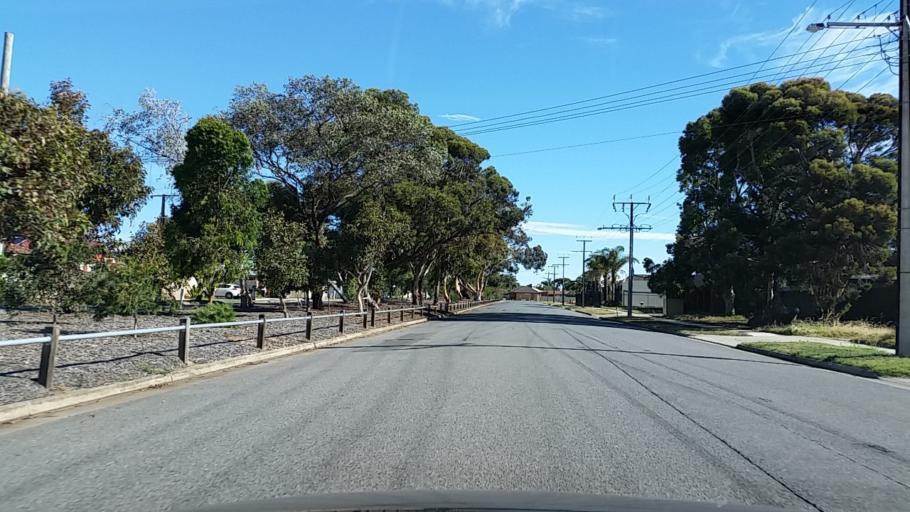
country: AU
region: South Australia
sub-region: Charles Sturt
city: Royal Park
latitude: -34.8662
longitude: 138.5073
